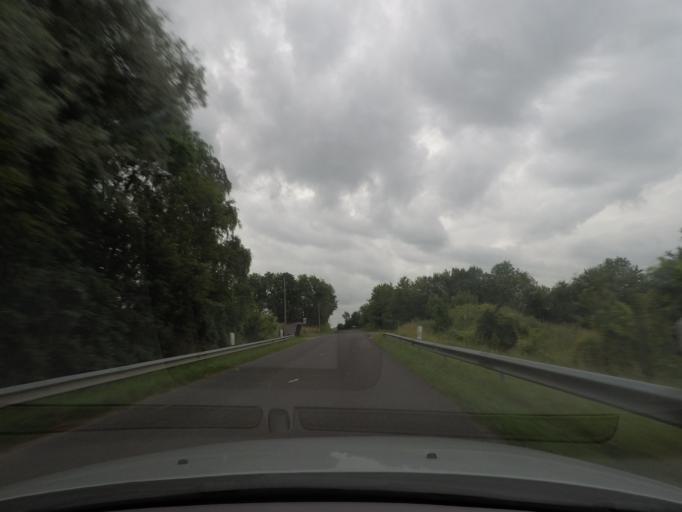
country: FR
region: Haute-Normandie
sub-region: Departement de la Seine-Maritime
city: Neufchatel-en-Bray
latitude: 49.7292
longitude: 1.4625
